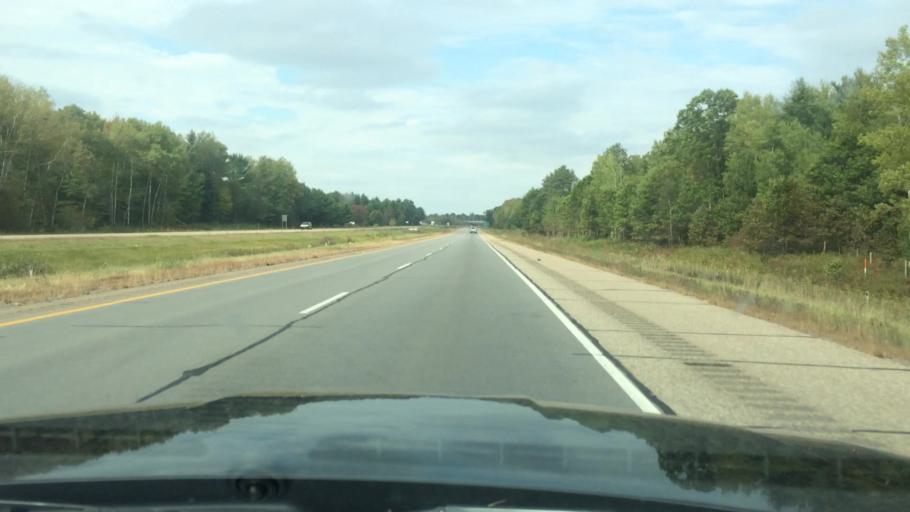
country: US
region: Wisconsin
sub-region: Marathon County
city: Mosinee
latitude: 44.7198
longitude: -89.6663
